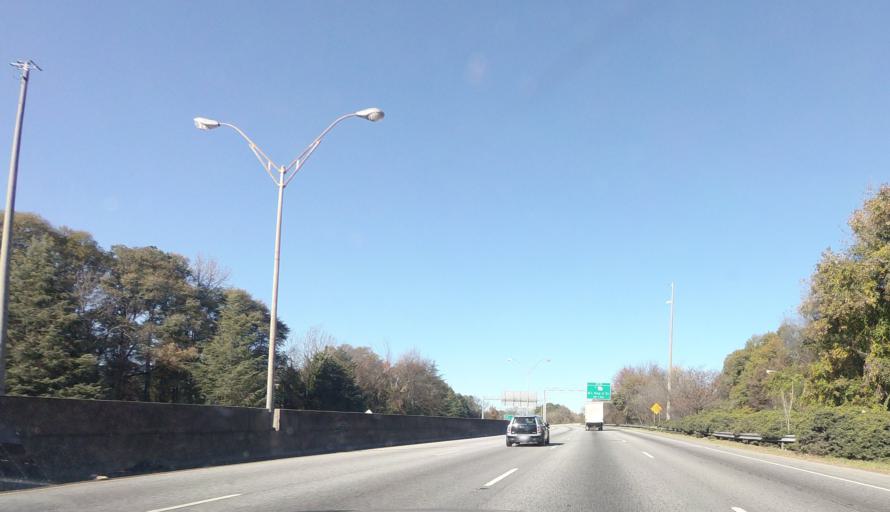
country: US
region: Georgia
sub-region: Fulton County
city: Atlanta
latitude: 33.7456
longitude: -84.4280
